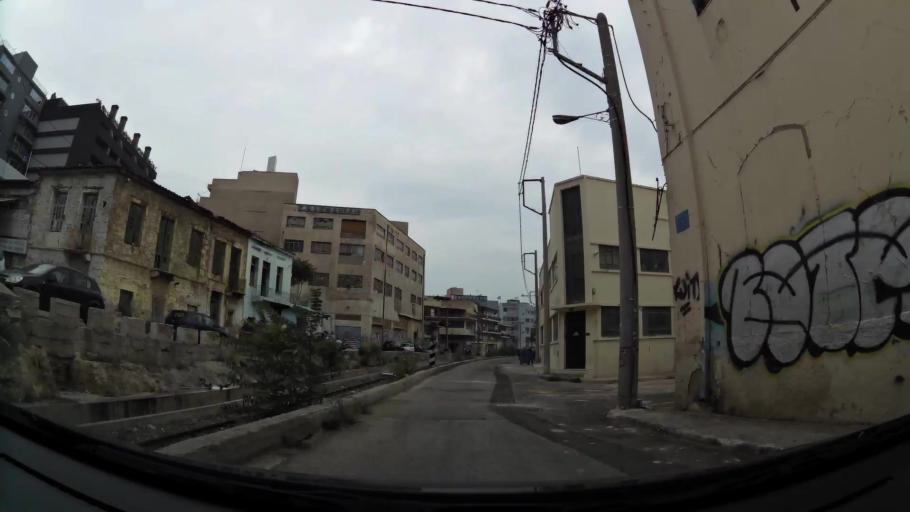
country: GR
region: Attica
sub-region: Nomos Attikis
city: Piraeus
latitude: 37.9513
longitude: 23.6355
